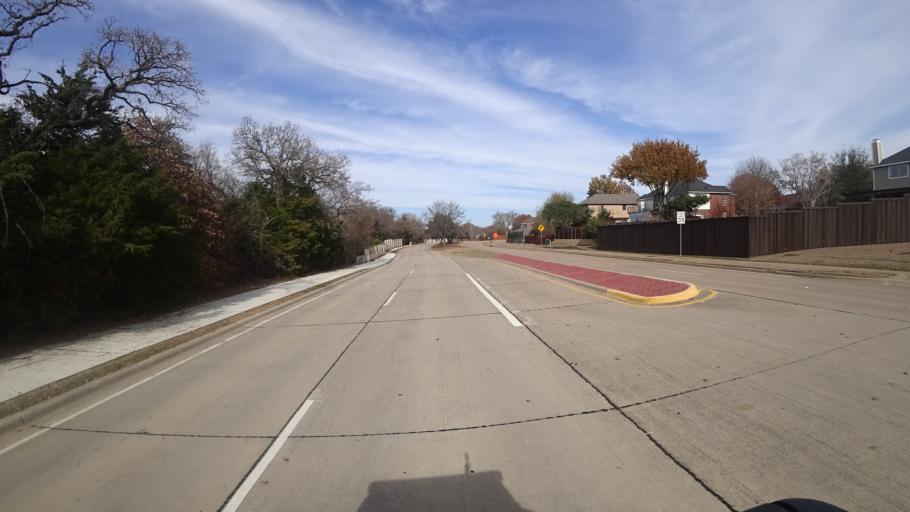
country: US
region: Texas
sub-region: Denton County
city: Highland Village
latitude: 33.0793
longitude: -97.0360
